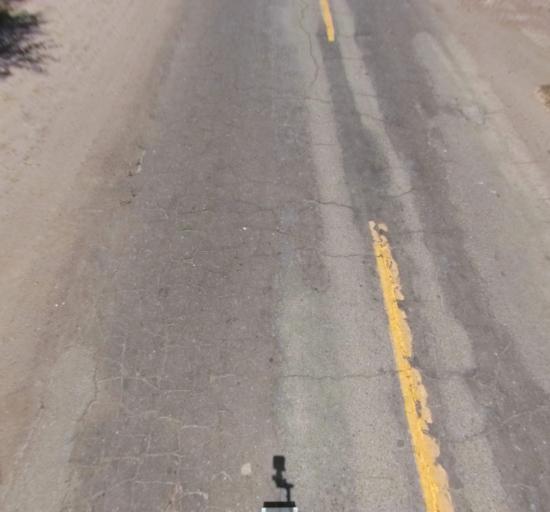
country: US
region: California
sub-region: Madera County
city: Chowchilla
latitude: 37.0355
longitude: -120.2925
